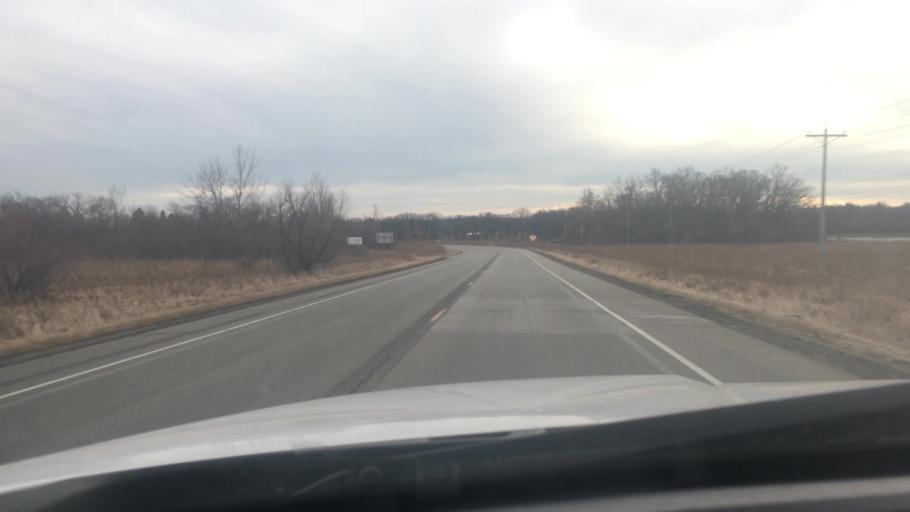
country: US
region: Minnesota
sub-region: Otter Tail County
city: Perham
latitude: 46.2969
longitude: -95.7181
